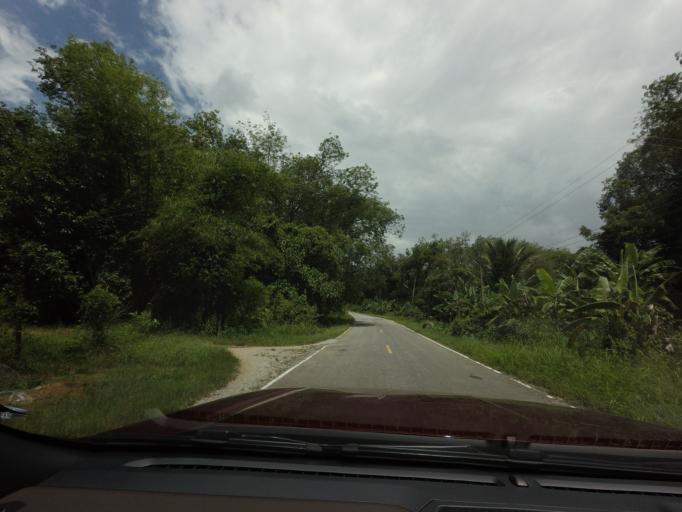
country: TH
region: Narathiwat
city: Chanae
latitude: 6.0464
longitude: 101.6900
